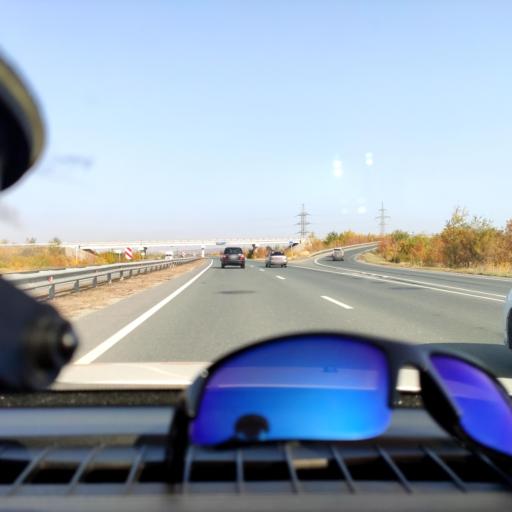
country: RU
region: Samara
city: Novokuybyshevsk
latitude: 53.0082
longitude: 49.9738
